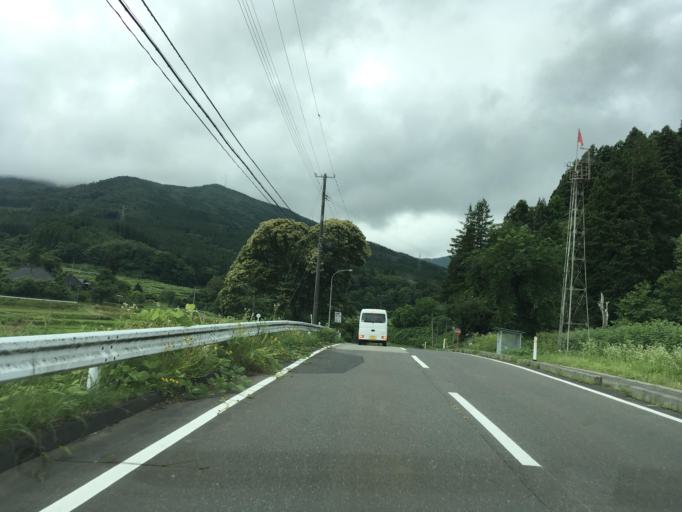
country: JP
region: Iwate
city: Ofunato
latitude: 38.8925
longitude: 141.4836
